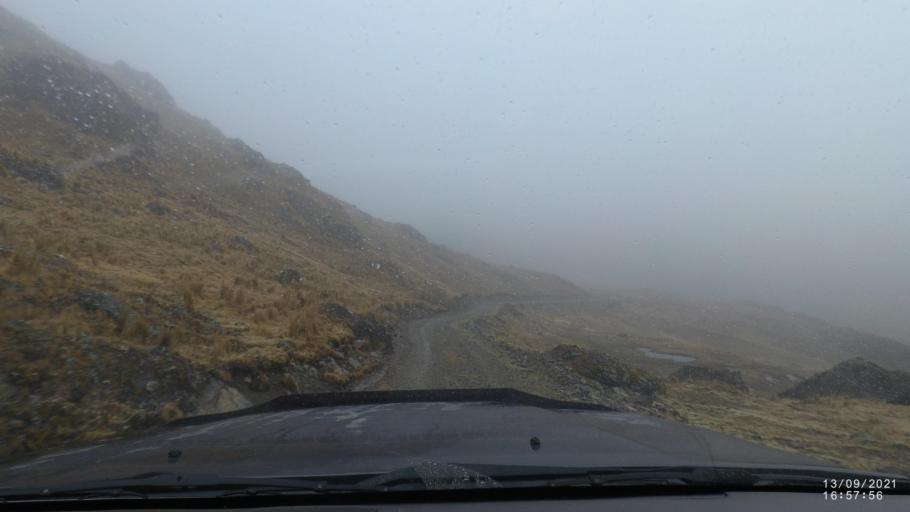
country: BO
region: Cochabamba
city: Colomi
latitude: -17.3070
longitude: -65.7154
